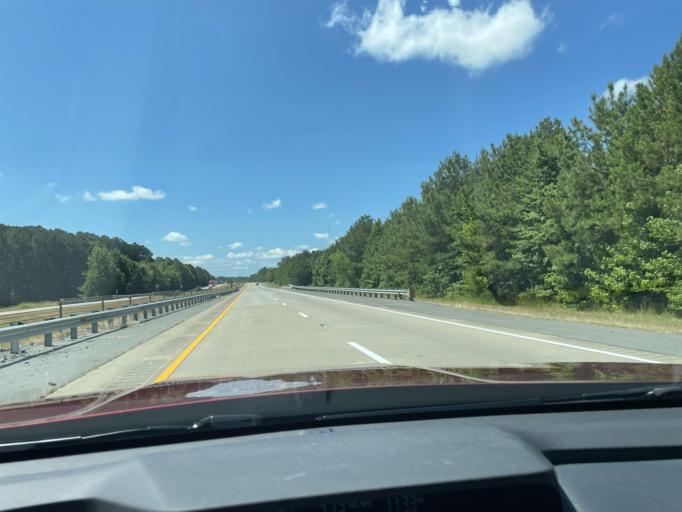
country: US
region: Arkansas
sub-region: Jefferson County
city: Redfield
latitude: 34.4901
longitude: -92.2087
